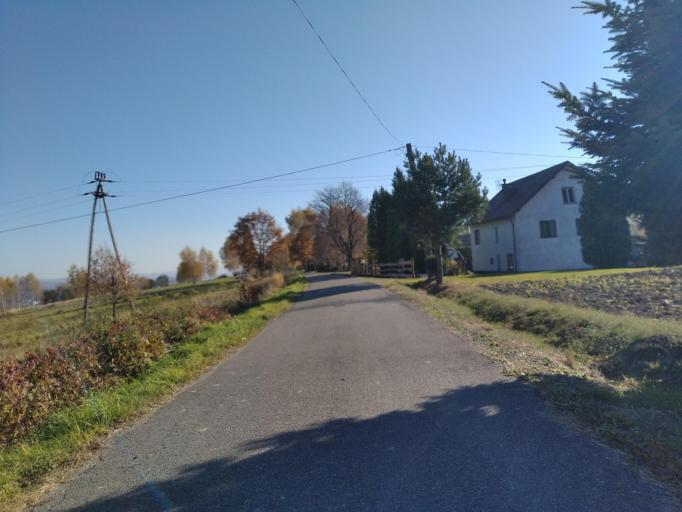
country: PL
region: Subcarpathian Voivodeship
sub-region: Powiat strzyzowski
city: Frysztak
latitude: 49.8615
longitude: 21.6113
